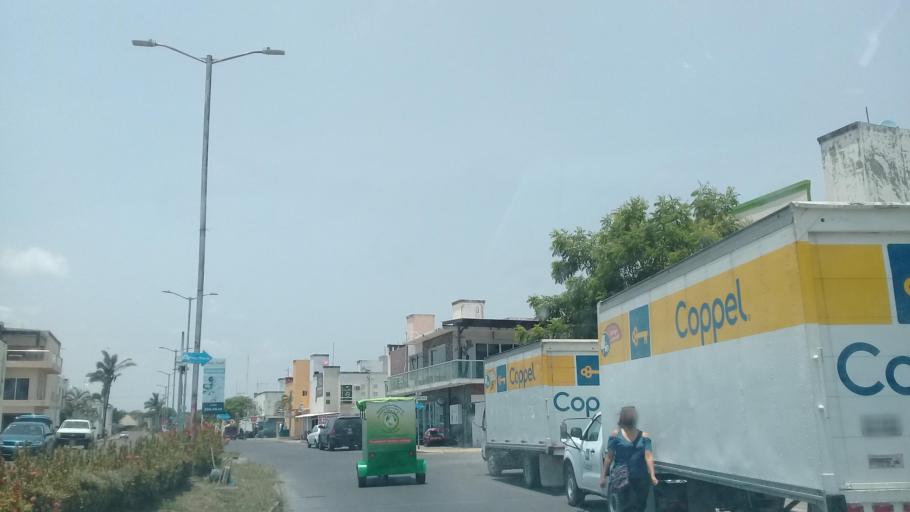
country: MX
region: Veracruz
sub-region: Veracruz
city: Hacienda Sotavento
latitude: 19.1303
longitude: -96.1751
